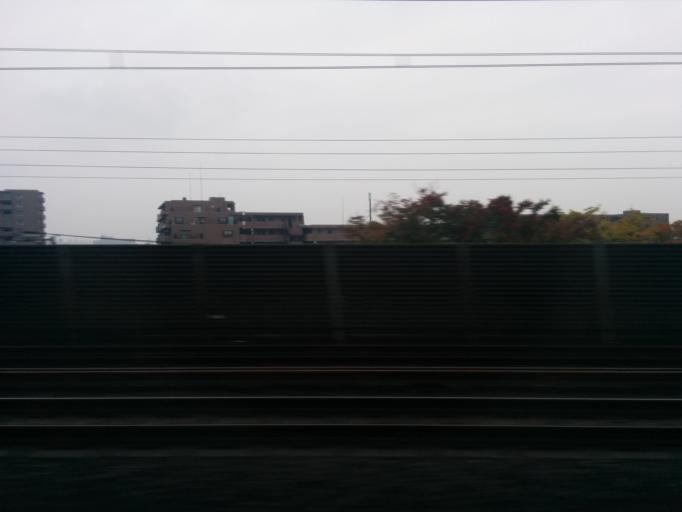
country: JP
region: Chiba
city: Chiba
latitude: 35.6512
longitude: 140.0784
